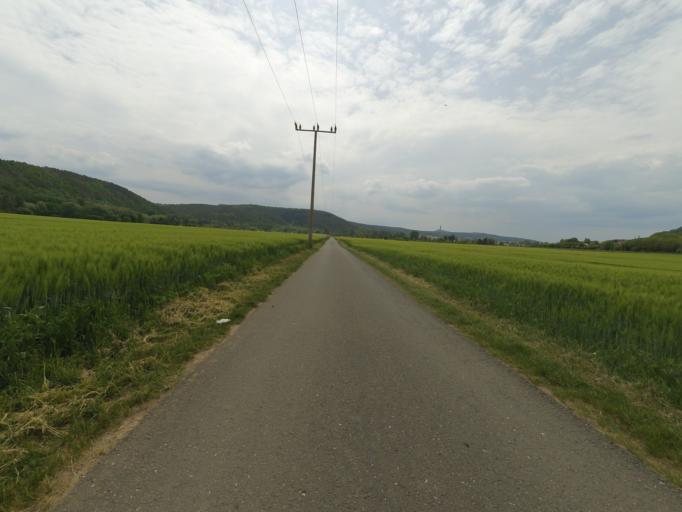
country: DE
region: Thuringia
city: Sulza
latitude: 50.8589
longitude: 11.6100
